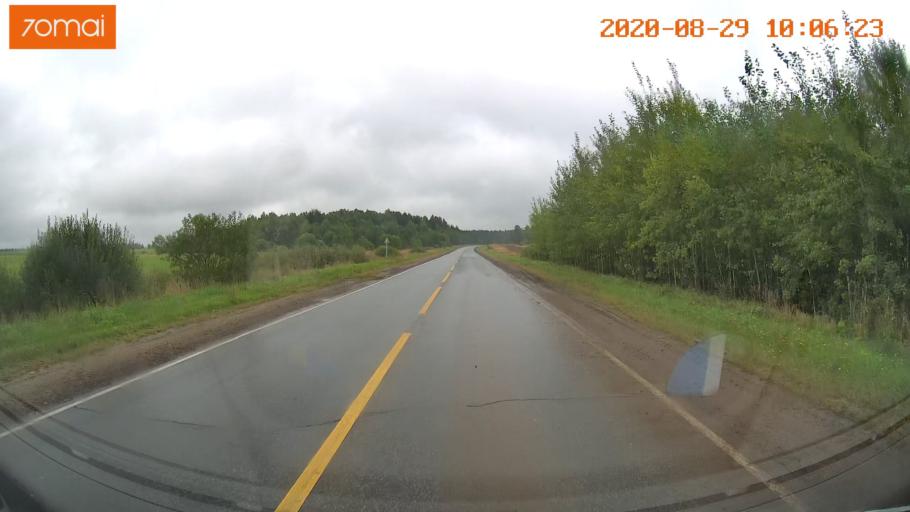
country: RU
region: Ivanovo
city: Kuznechikha
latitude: 57.3888
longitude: 42.5442
